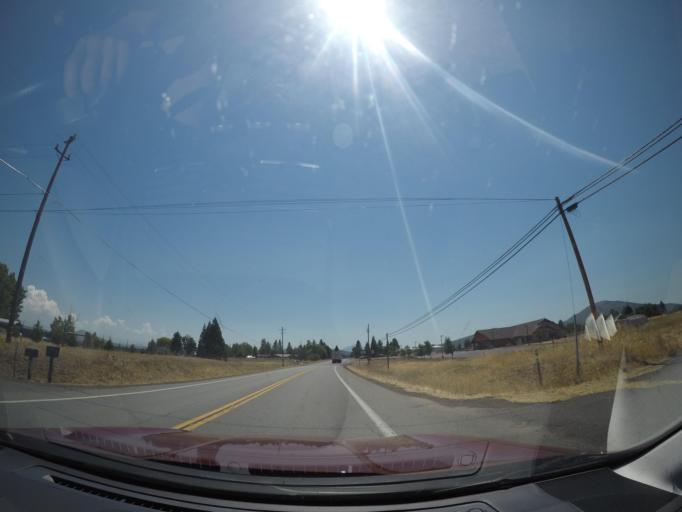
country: US
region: California
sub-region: Shasta County
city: Burney
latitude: 41.0291
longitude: -121.4202
